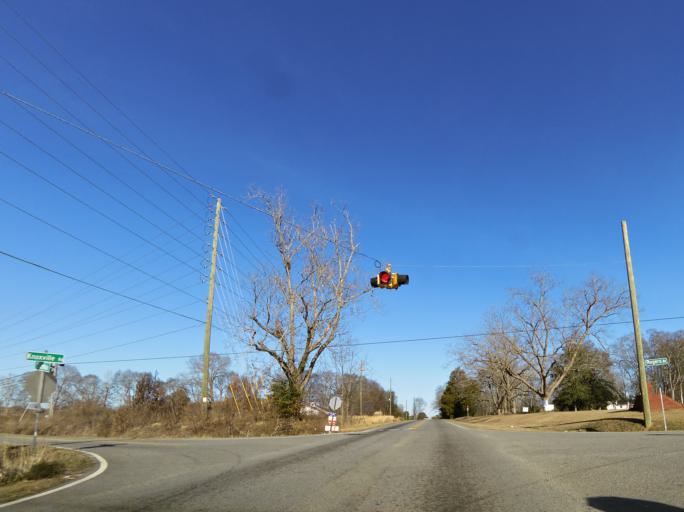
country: US
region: Georgia
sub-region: Bibb County
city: West Point
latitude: 32.7768
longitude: -83.8217
